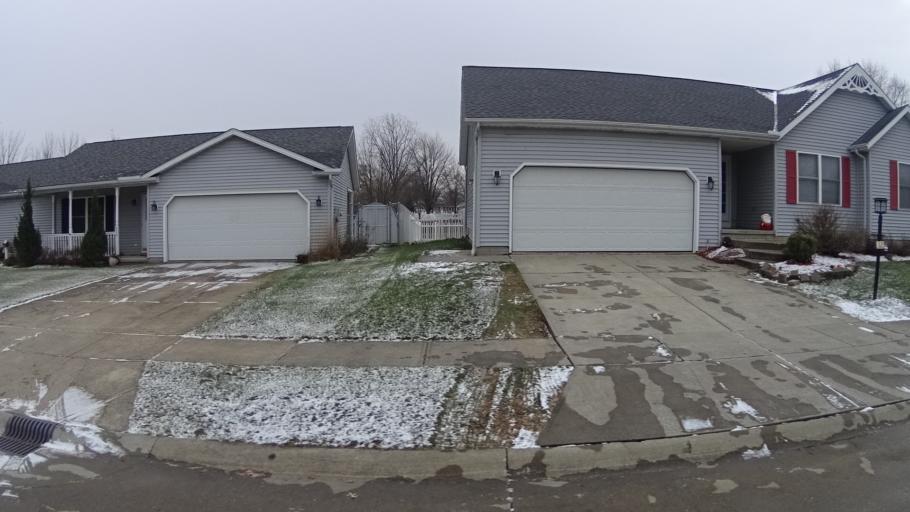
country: US
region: Ohio
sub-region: Lorain County
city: Lagrange
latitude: 41.2032
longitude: -82.1472
